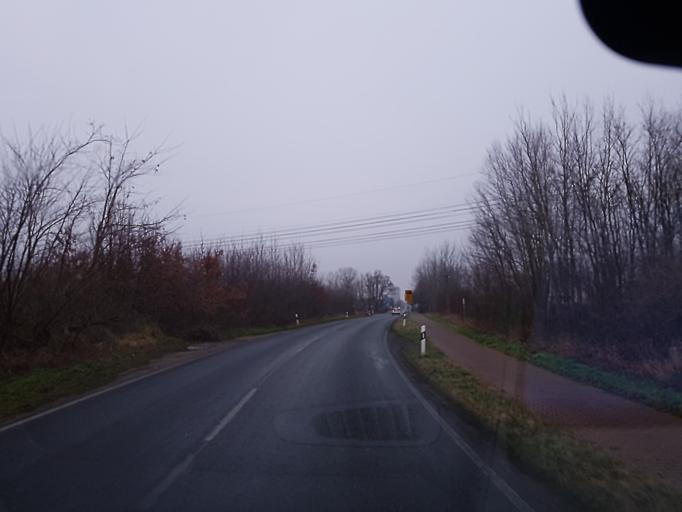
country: DE
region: Brandenburg
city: Lubbenau
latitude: 51.8499
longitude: 13.9485
